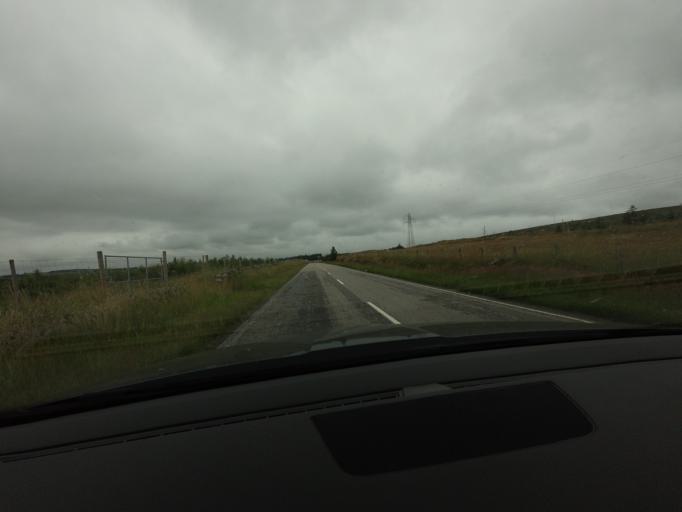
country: GB
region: Scotland
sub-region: Highland
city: Alness
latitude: 58.0528
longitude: -4.4201
